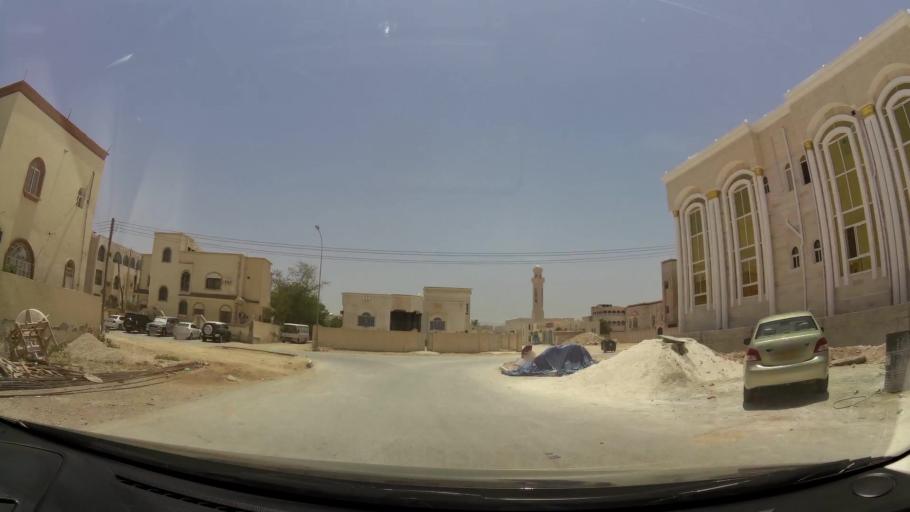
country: OM
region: Zufar
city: Salalah
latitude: 17.0721
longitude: 54.1586
